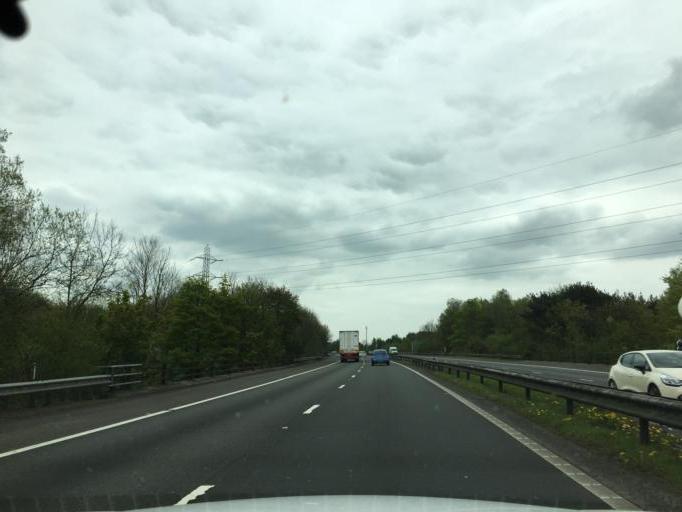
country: GB
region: Wales
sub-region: Cardiff
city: Radyr
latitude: 51.5261
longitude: -3.2461
